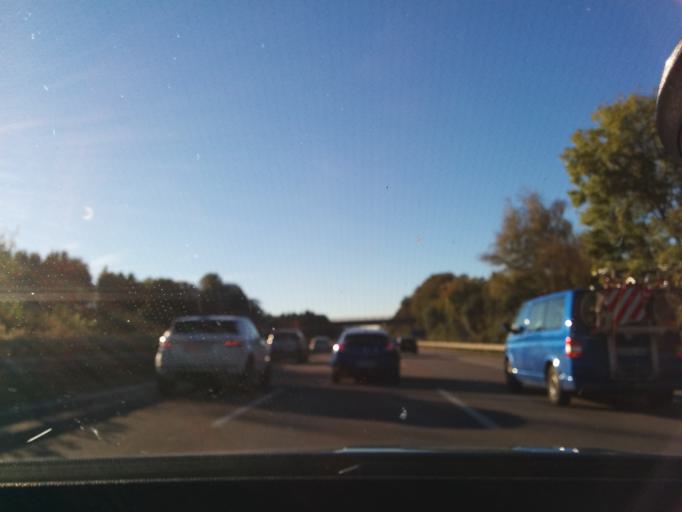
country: DE
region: Bavaria
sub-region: Upper Bavaria
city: Kolbermoor
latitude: 47.8127
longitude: 12.0788
